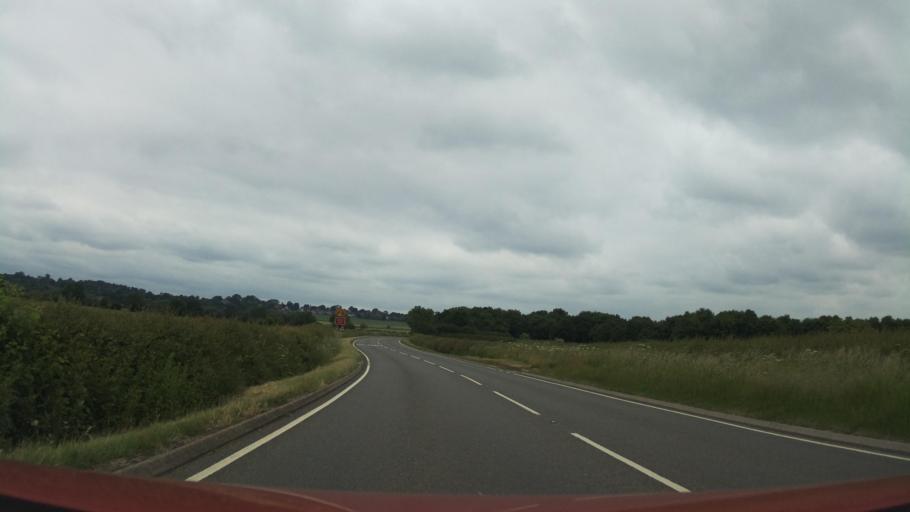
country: GB
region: England
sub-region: Leicestershire
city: Melton Mowbray
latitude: 52.7319
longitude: -0.8485
